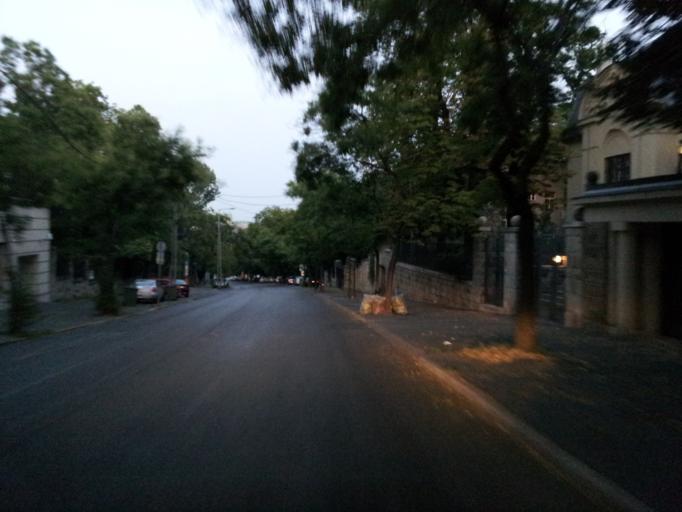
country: HU
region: Budapest
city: Budapest XII. keruelet
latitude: 47.4980
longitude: 19.0171
